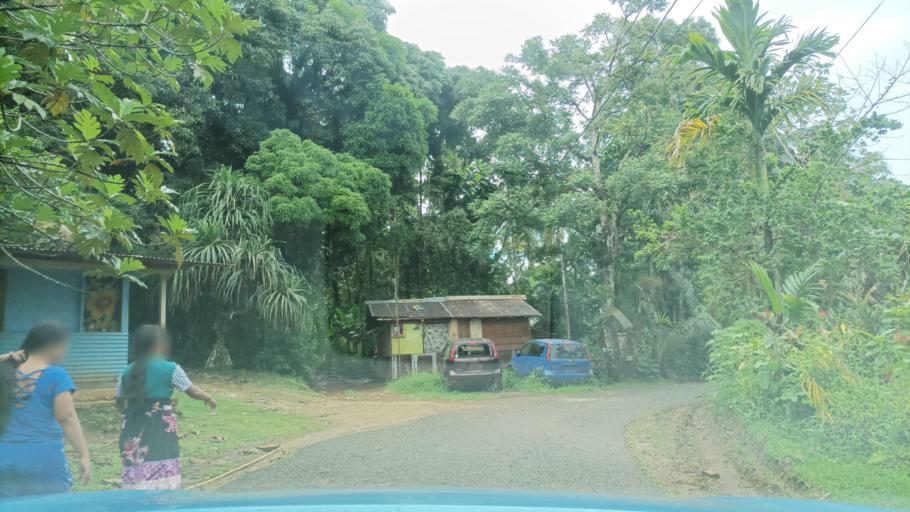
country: FM
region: Pohnpei
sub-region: Sokehs Municipality
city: Palikir - National Government Center
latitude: 6.8363
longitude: 158.1727
